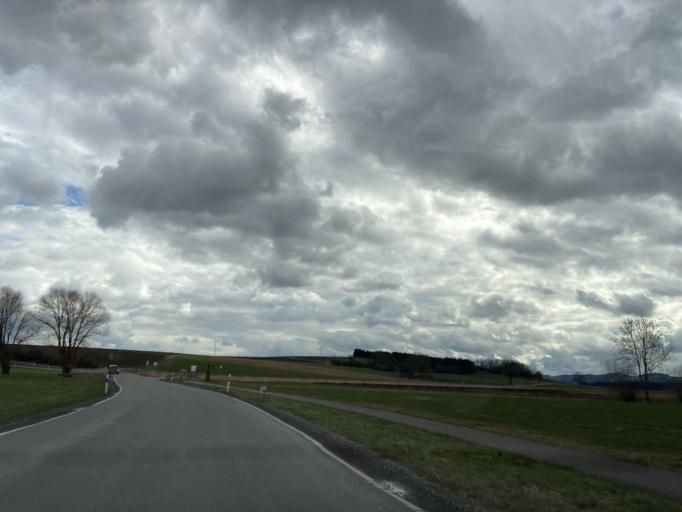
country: DE
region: Baden-Wuerttemberg
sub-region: Tuebingen Region
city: Ostrach
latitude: 47.9473
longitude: 9.3880
